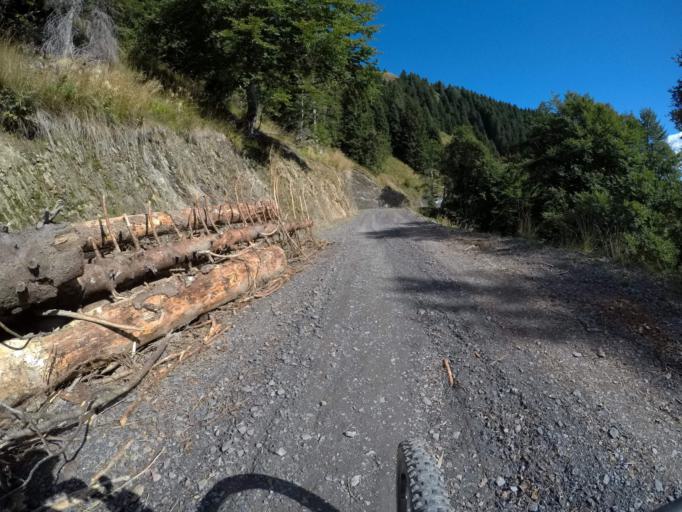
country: IT
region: Friuli Venezia Giulia
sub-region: Provincia di Udine
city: Ligosullo
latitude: 46.5681
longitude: 13.0895
